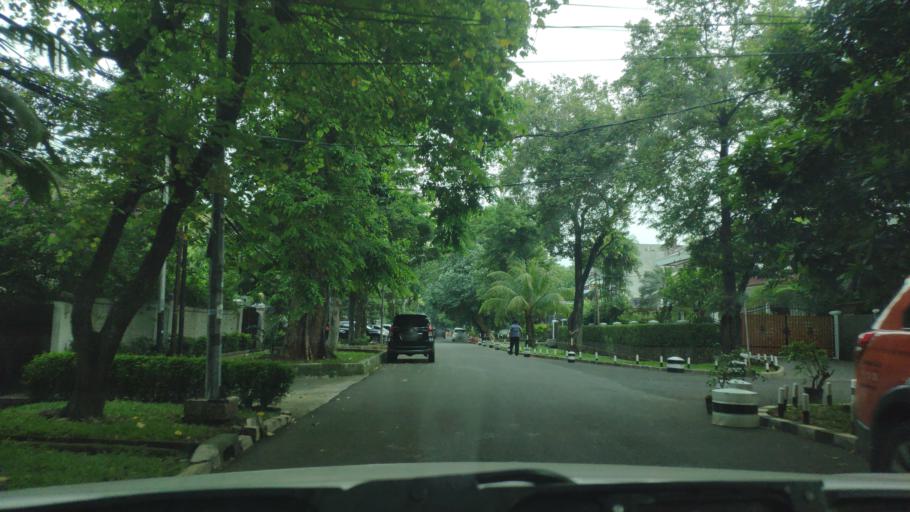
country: ID
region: Jakarta Raya
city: Jakarta
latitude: -6.2362
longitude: 106.8032
